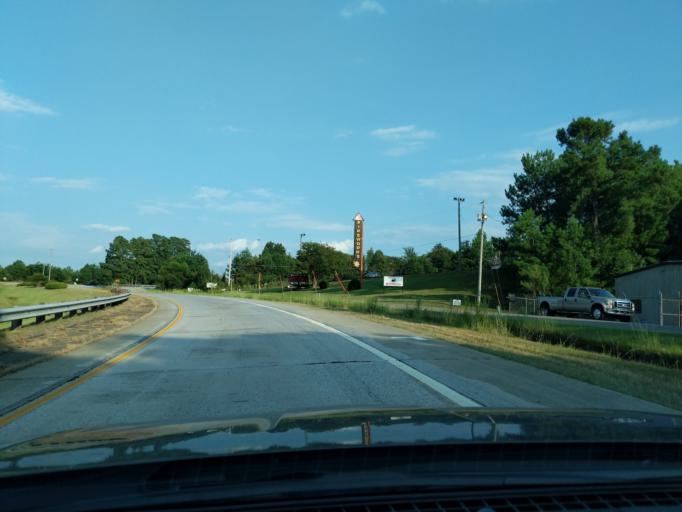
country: US
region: South Carolina
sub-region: Aiken County
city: North Augusta
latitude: 33.5382
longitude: -81.9924
